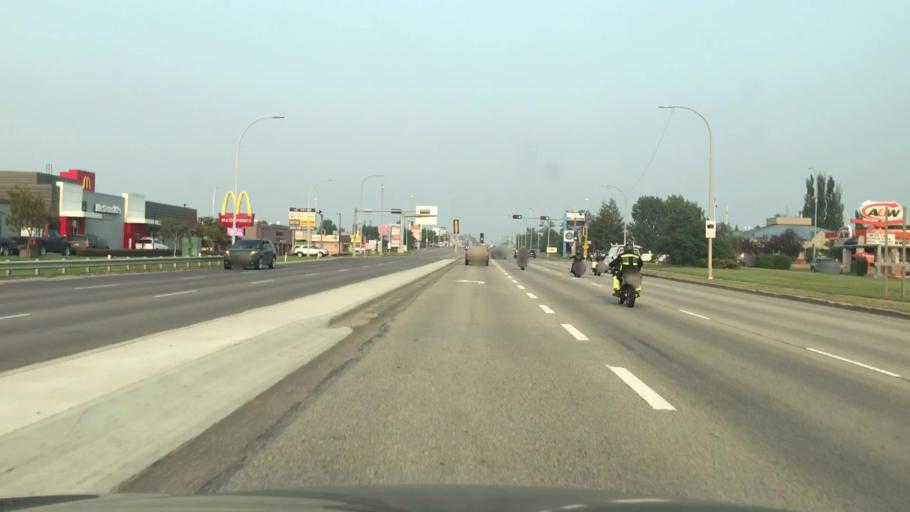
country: CA
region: Alberta
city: Sherwood Park
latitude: 53.5121
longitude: -113.3320
